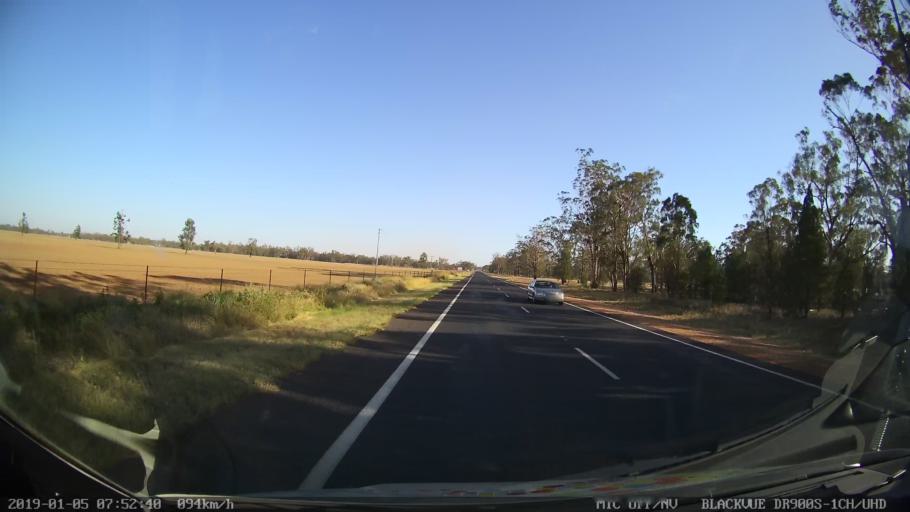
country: AU
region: New South Wales
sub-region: Gilgandra
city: Gilgandra
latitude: -31.7551
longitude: 148.6405
